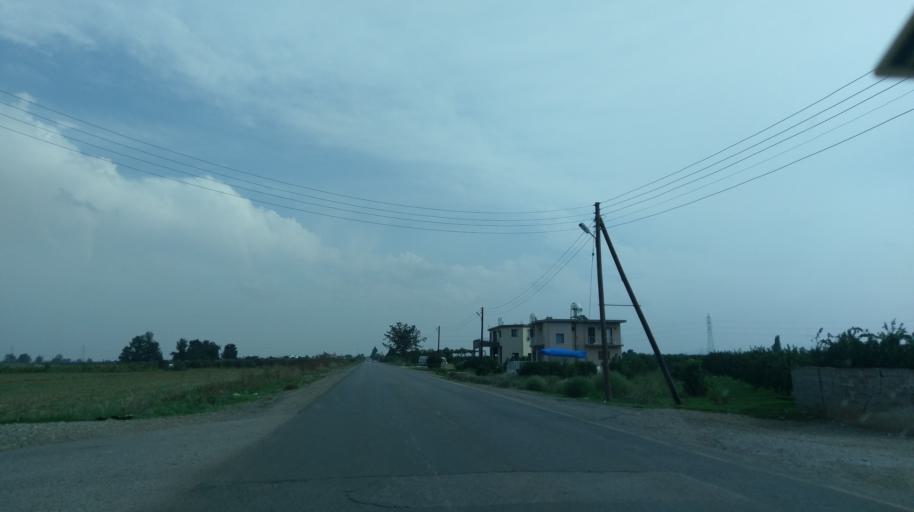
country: CY
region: Lefkosia
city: Morfou
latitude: 35.1866
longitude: 33.0119
